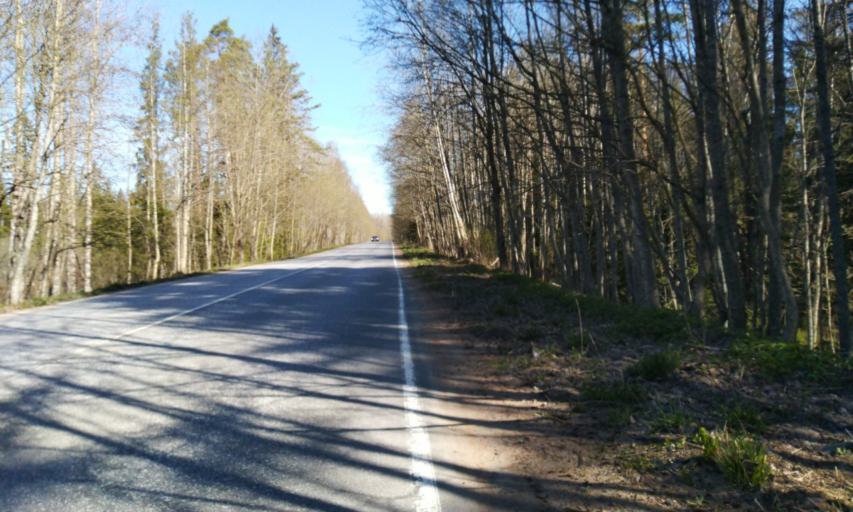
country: RU
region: Leningrad
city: Garbolovo
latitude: 60.3644
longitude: 30.4423
